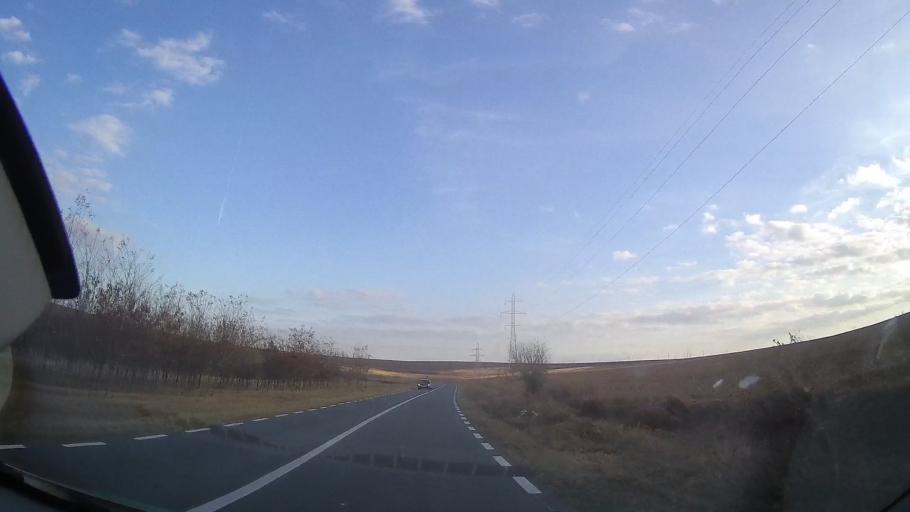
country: RO
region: Constanta
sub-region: Comuna Chirnogeni
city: Plopeni
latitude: 43.9565
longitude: 28.1489
